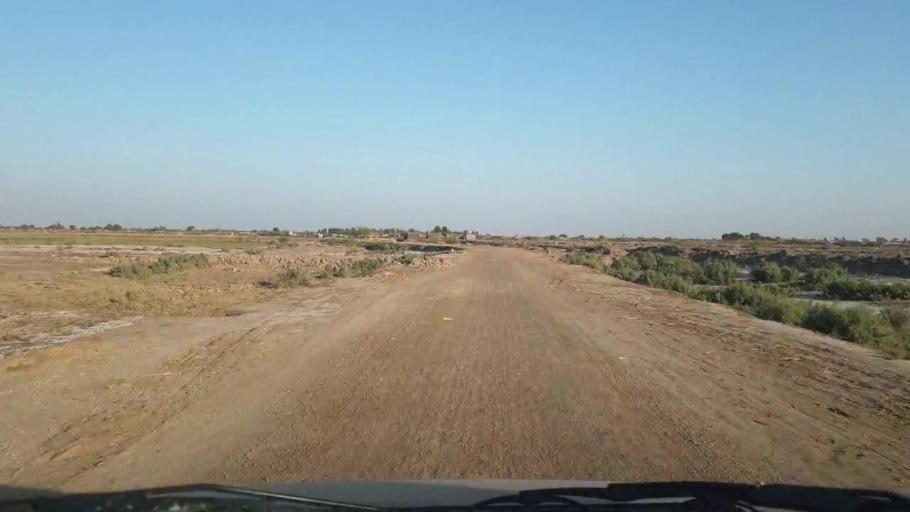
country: PK
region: Sindh
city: Samaro
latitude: 25.3197
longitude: 69.2964
